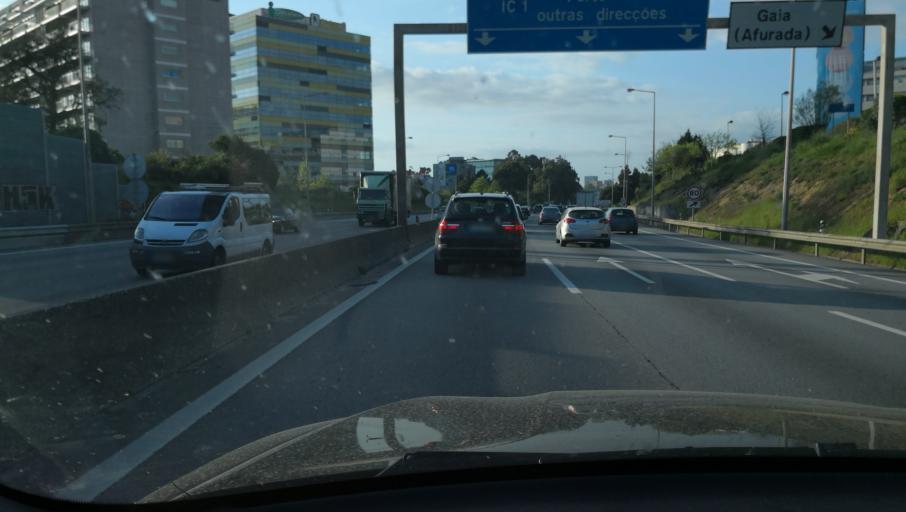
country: PT
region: Porto
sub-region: Vila Nova de Gaia
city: Canidelo
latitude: 41.1411
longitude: -8.6384
